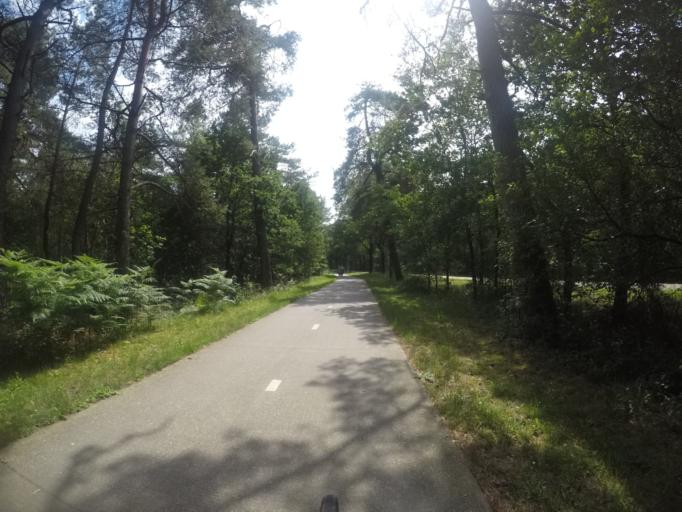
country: NL
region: Drenthe
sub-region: Gemeente Westerveld
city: Dwingeloo
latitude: 52.8809
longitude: 6.3239
